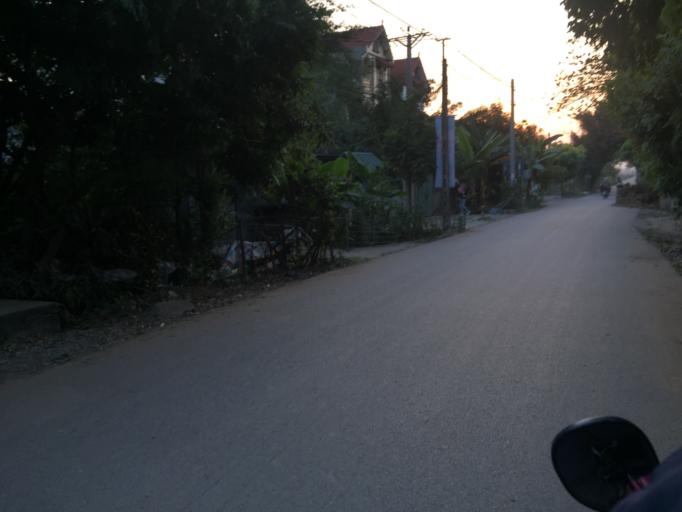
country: VN
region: Ha Noi
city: Chuc Son
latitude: 20.8927
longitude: 105.7232
